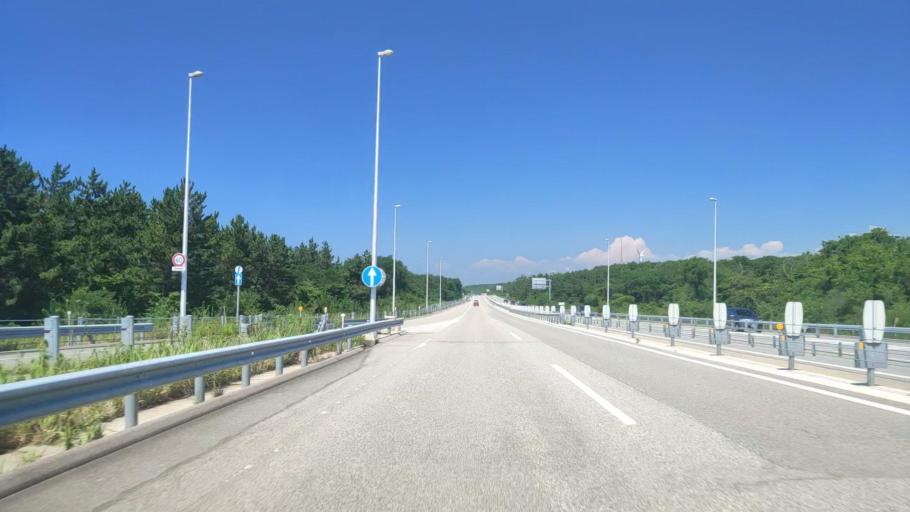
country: JP
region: Ishikawa
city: Kanazawa-shi
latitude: 36.6534
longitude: 136.6366
